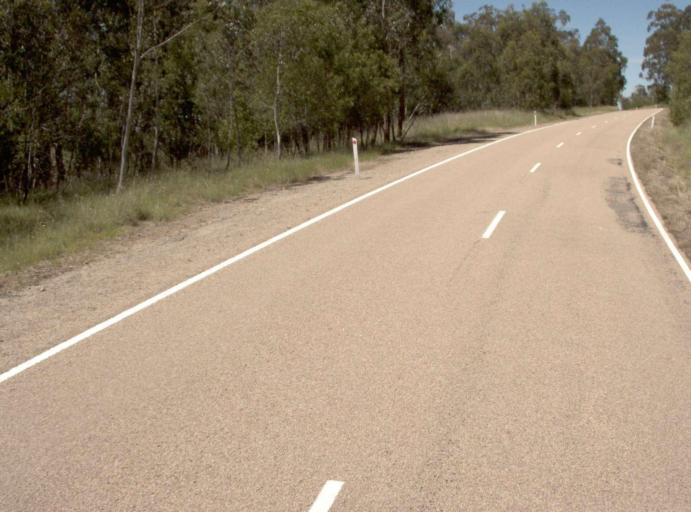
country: AU
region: Victoria
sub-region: East Gippsland
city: Lakes Entrance
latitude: -37.2112
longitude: 148.2695
